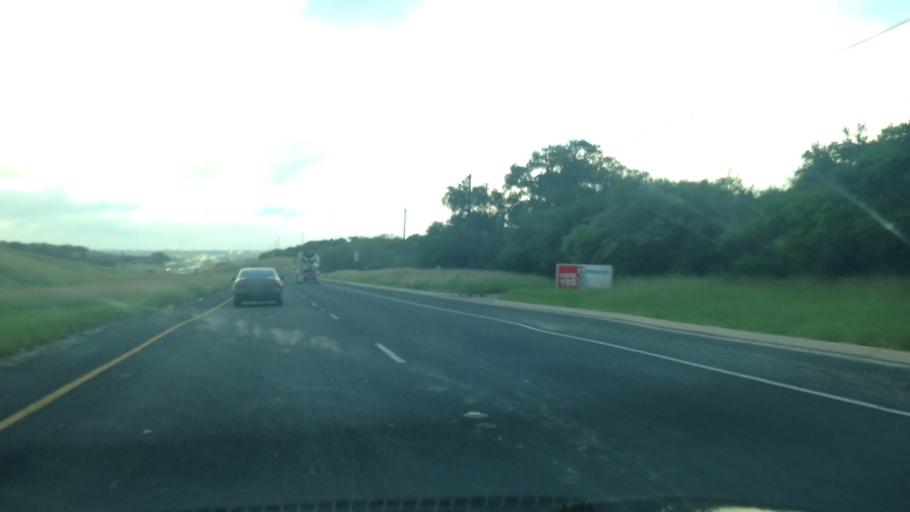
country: US
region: Texas
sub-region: Bexar County
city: Live Oak
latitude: 29.6030
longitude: -98.3893
